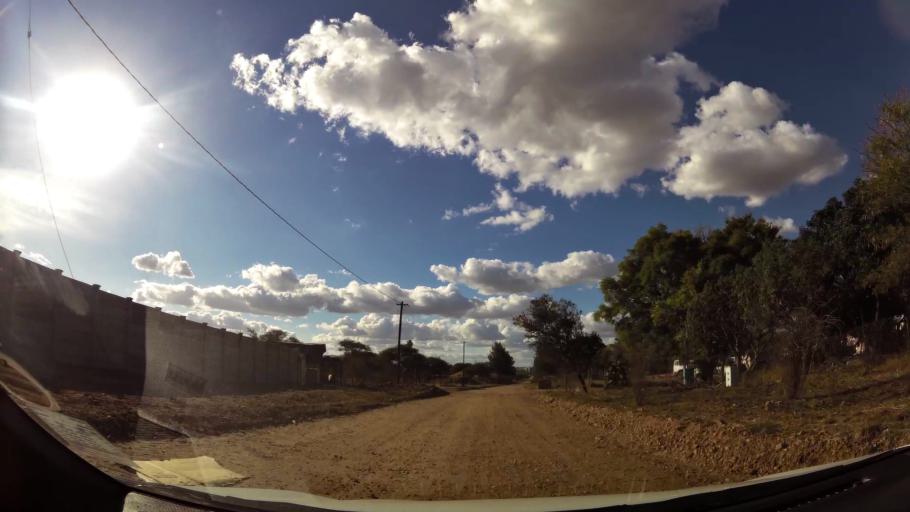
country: ZA
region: Limpopo
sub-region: Capricorn District Municipality
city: Polokwane
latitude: -23.9344
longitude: 29.4446
